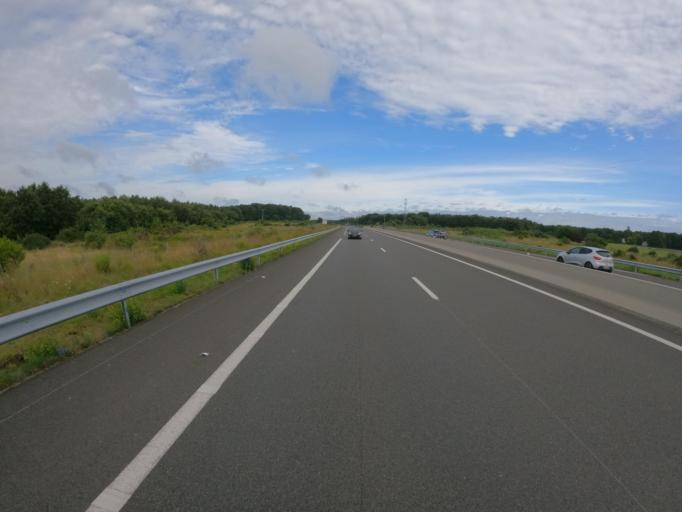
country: FR
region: Centre
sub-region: Departement d'Indre-et-Loire
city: Langeais
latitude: 47.3417
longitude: 0.4217
